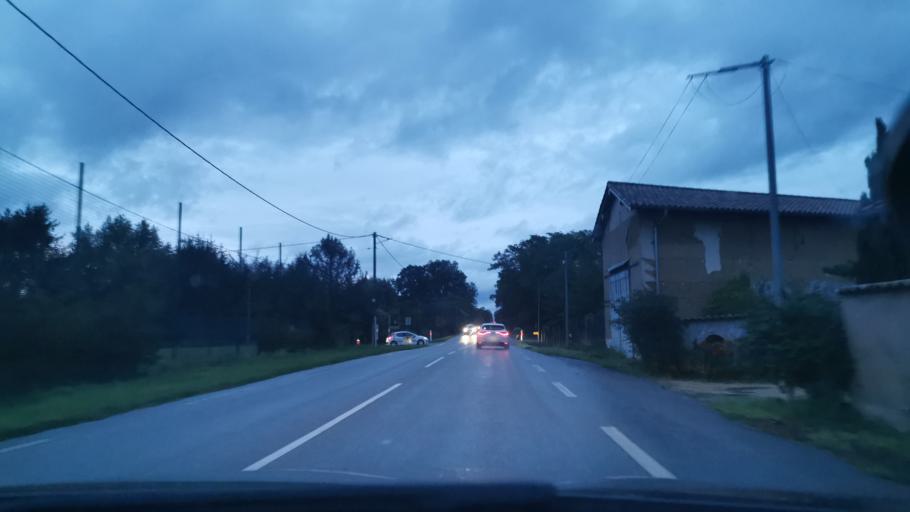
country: FR
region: Rhone-Alpes
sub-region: Departement de l'Ain
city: Crottet
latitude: 46.2758
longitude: 4.8994
